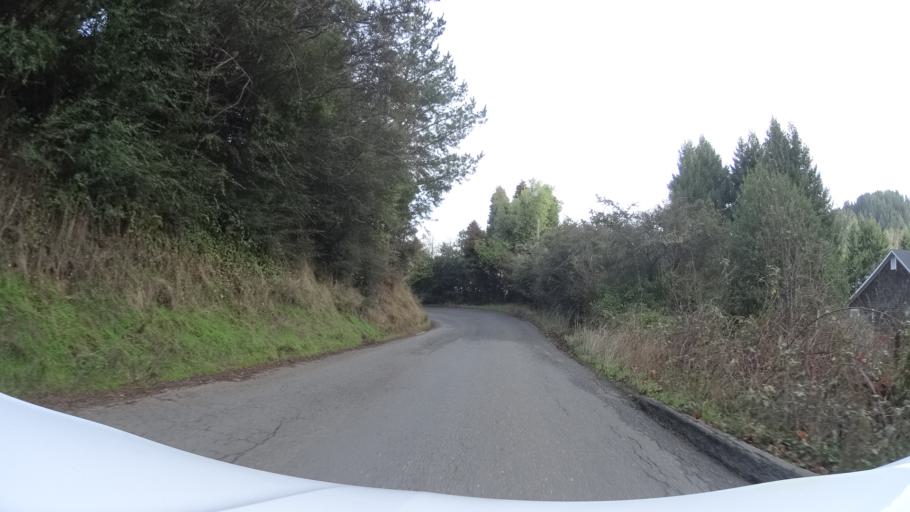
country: US
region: California
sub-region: Humboldt County
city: Ferndale
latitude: 40.5757
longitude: -124.2677
